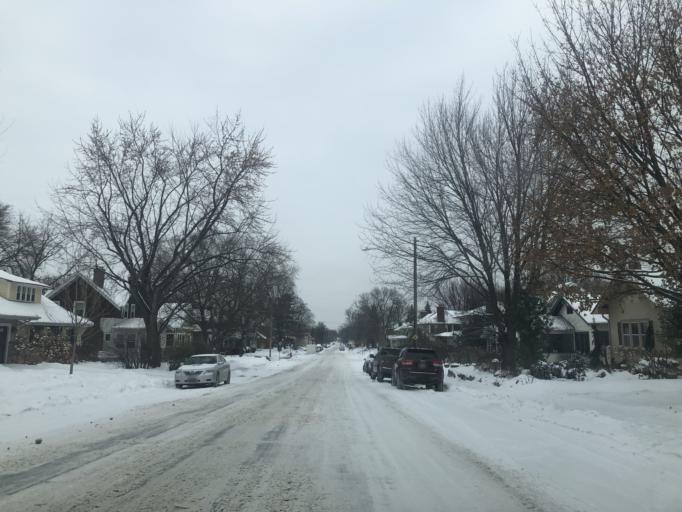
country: US
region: Minnesota
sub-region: Hennepin County
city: Richfield
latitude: 44.9169
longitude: -93.2909
